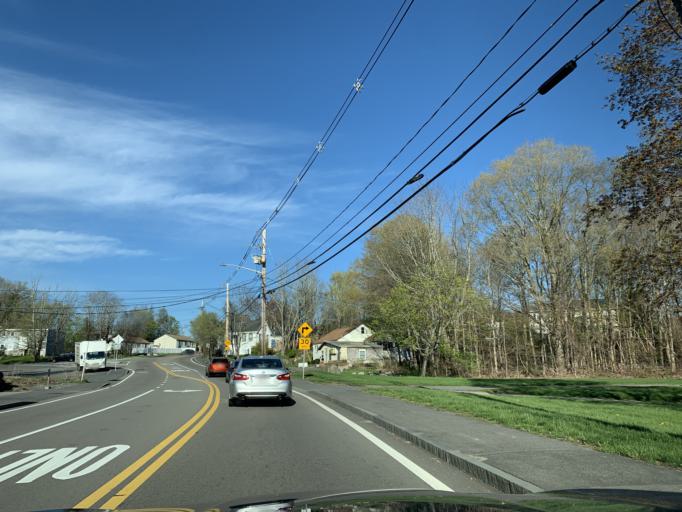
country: US
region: Massachusetts
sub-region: Norfolk County
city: Stoughton
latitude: 42.1307
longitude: -71.1289
